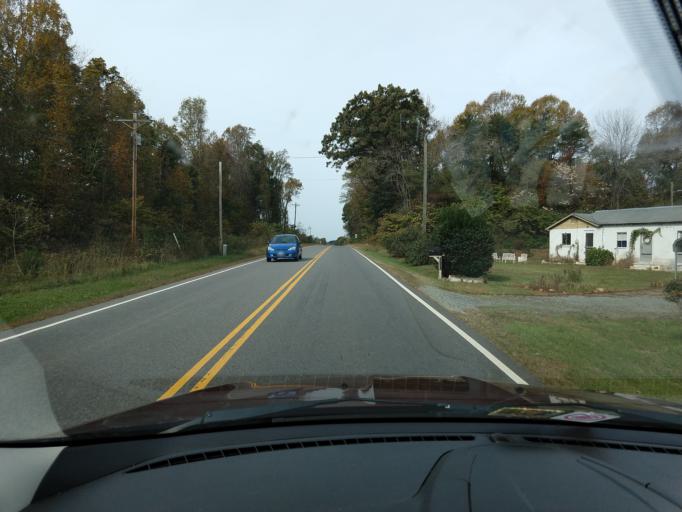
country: US
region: Virginia
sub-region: Franklin County
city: Union Hall
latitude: 36.9571
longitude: -79.5646
